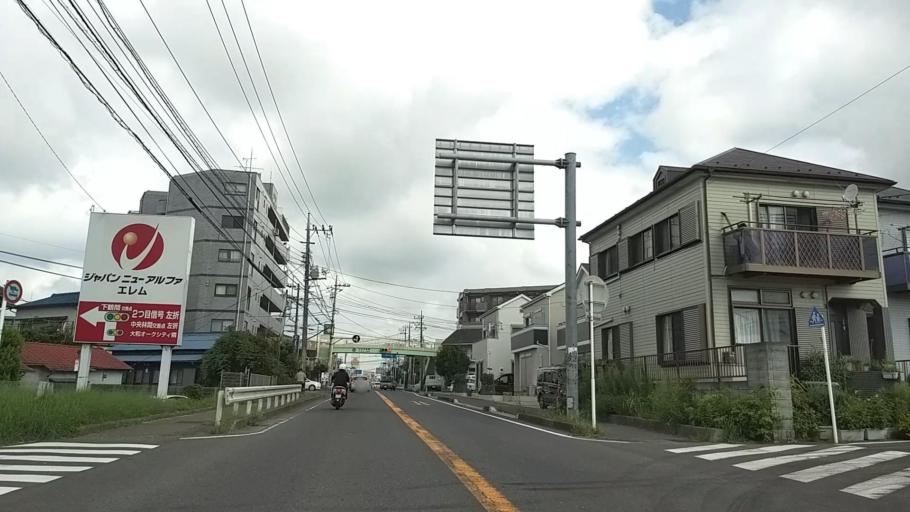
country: JP
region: Kanagawa
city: Minami-rinkan
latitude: 35.5033
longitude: 139.4653
